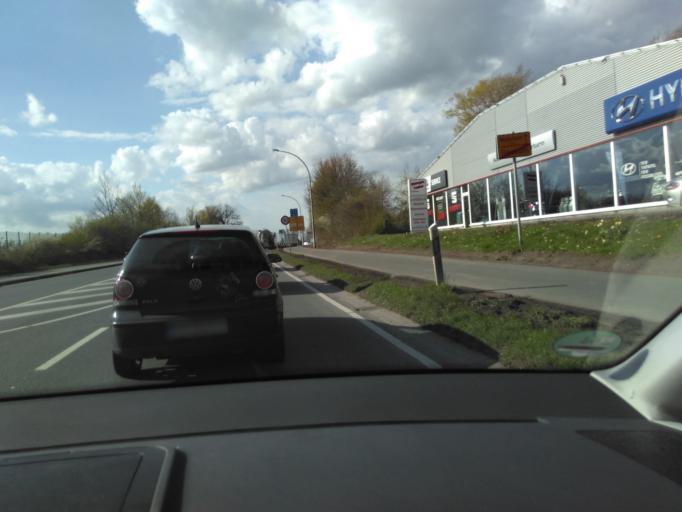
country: DE
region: North Rhine-Westphalia
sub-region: Regierungsbezirk Munster
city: Beckum
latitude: 51.7727
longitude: 8.0366
